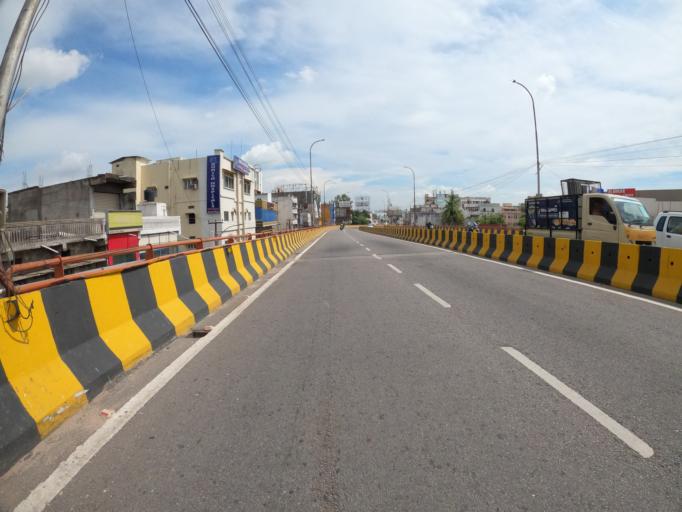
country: IN
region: Telangana
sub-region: Hyderabad
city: Hyderabad
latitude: 17.3767
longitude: 78.4203
